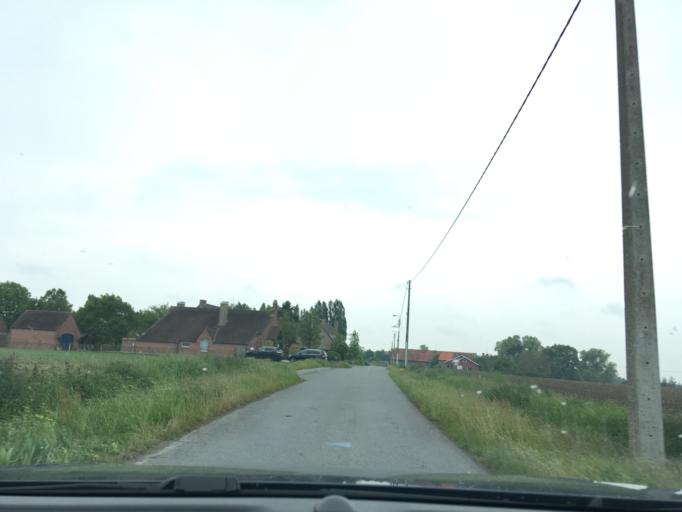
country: BE
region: Flanders
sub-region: Provincie West-Vlaanderen
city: Hooglede
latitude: 51.0002
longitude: 3.1012
